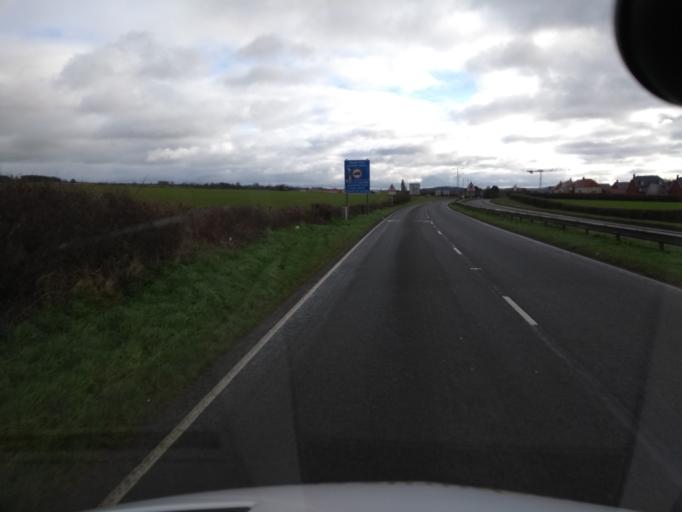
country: GB
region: England
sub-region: Dorset
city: Sherborne
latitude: 50.9474
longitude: -2.5393
